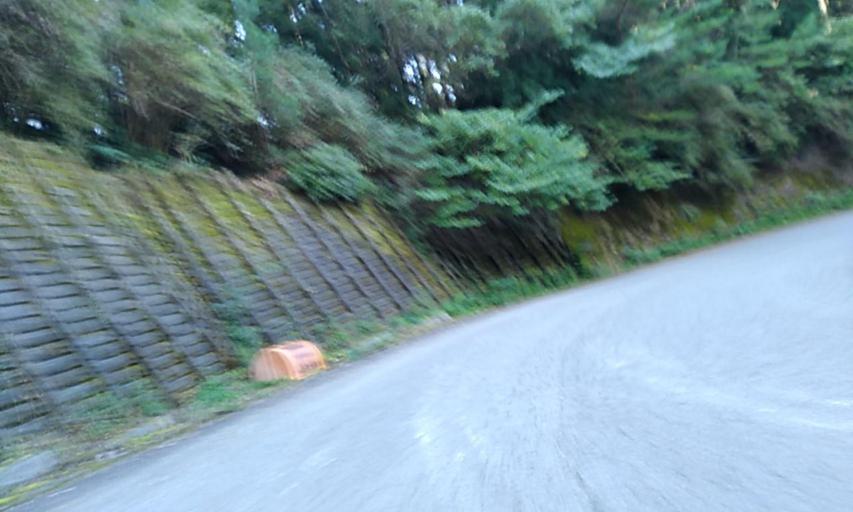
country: JP
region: Wakayama
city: Iwade
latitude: 34.1119
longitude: 135.3456
